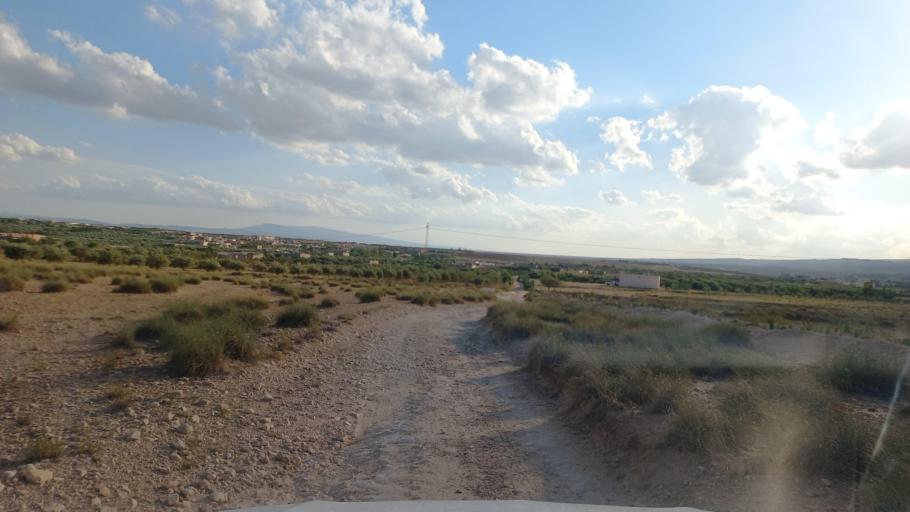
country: TN
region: Al Qasrayn
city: Sbiba
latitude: 35.3890
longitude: 9.0555
